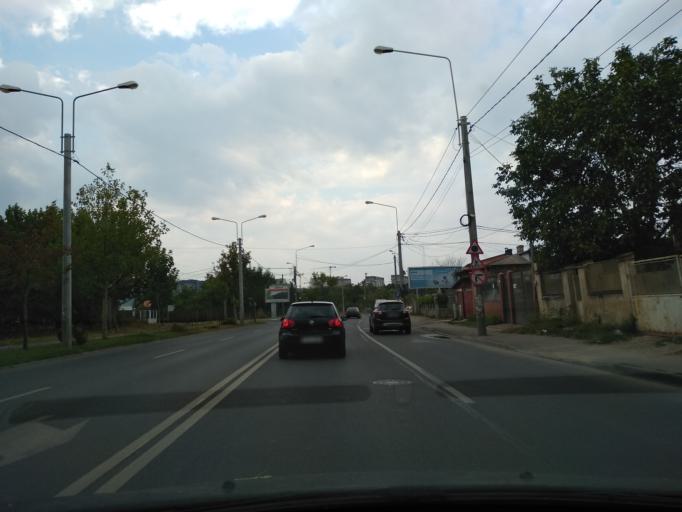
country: RO
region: Ilfov
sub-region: Comuna Fundeni-Dobroesti
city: Fundeni
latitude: 44.4708
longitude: 26.1252
